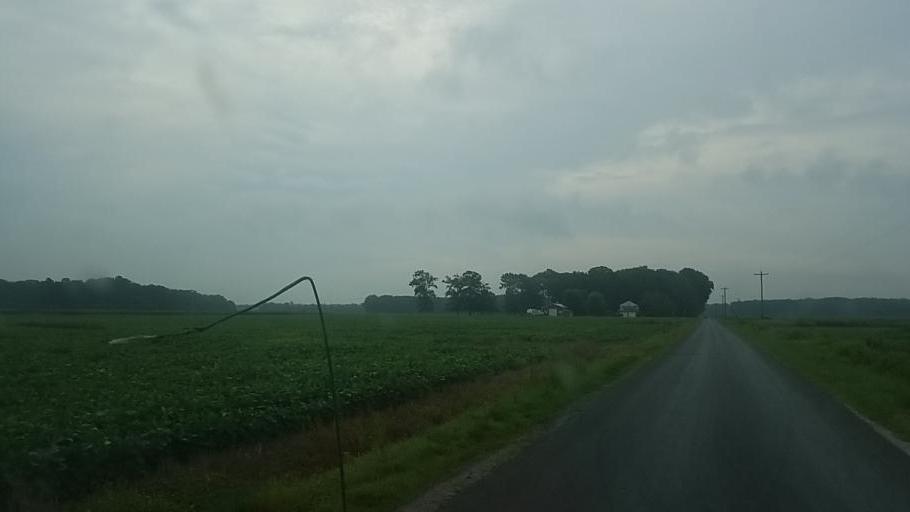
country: US
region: Delaware
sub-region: Sussex County
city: Selbyville
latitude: 38.4426
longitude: -75.2660
